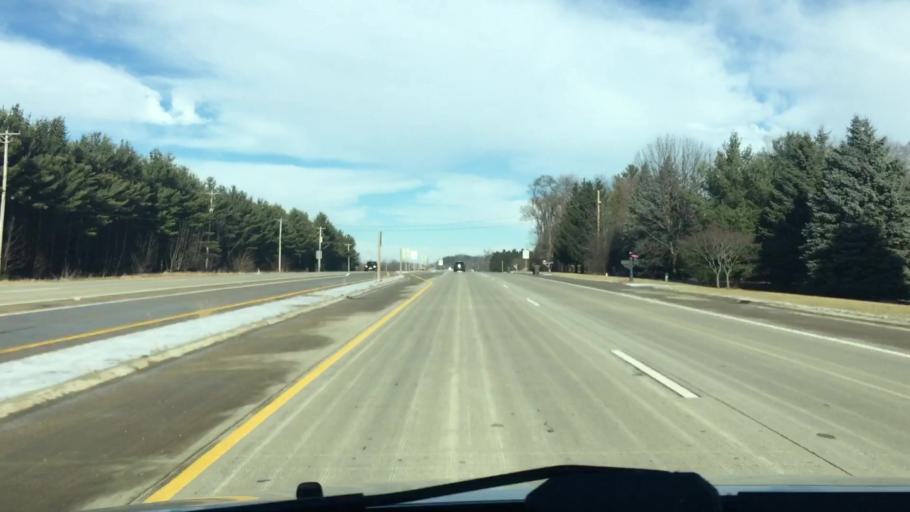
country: US
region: Wisconsin
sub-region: Waukesha County
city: Mukwonago
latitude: 42.8871
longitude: -88.3435
